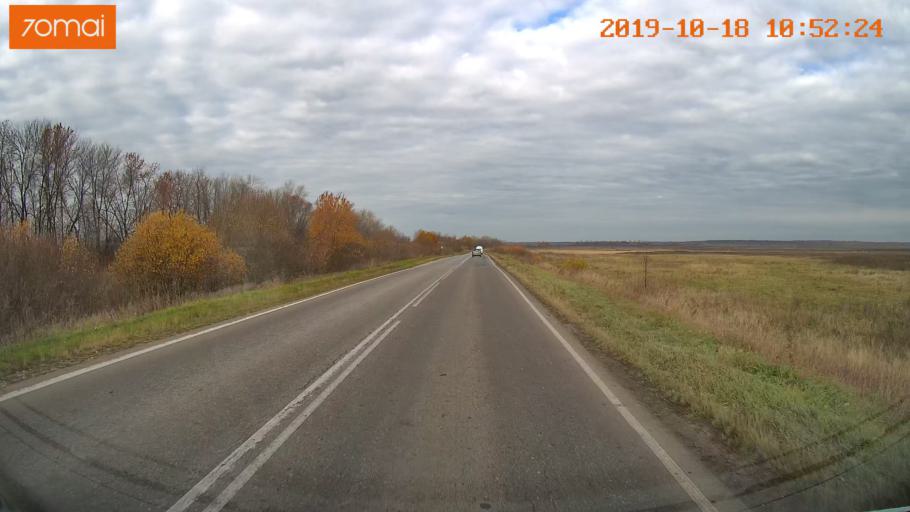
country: RU
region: Tula
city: Yepifan'
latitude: 53.7659
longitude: 38.6518
